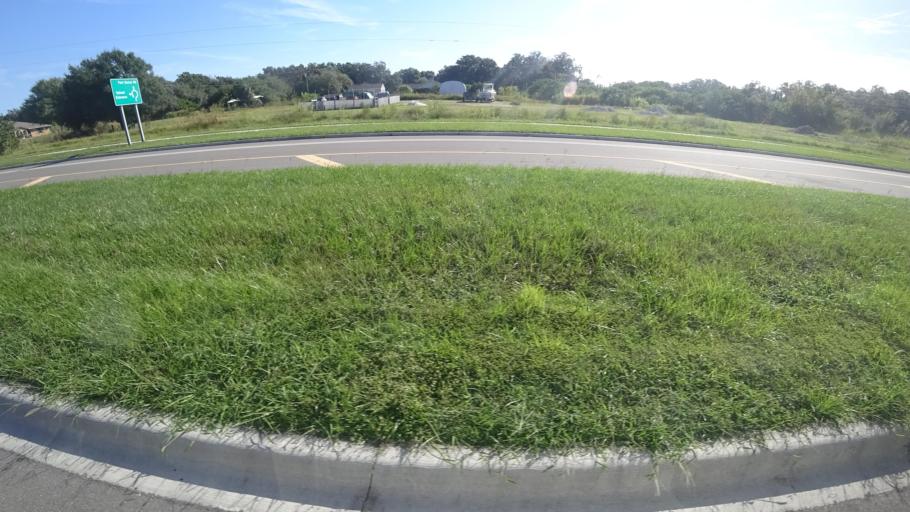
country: US
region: Florida
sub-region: Manatee County
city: Ellenton
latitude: 27.5773
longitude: -82.4352
